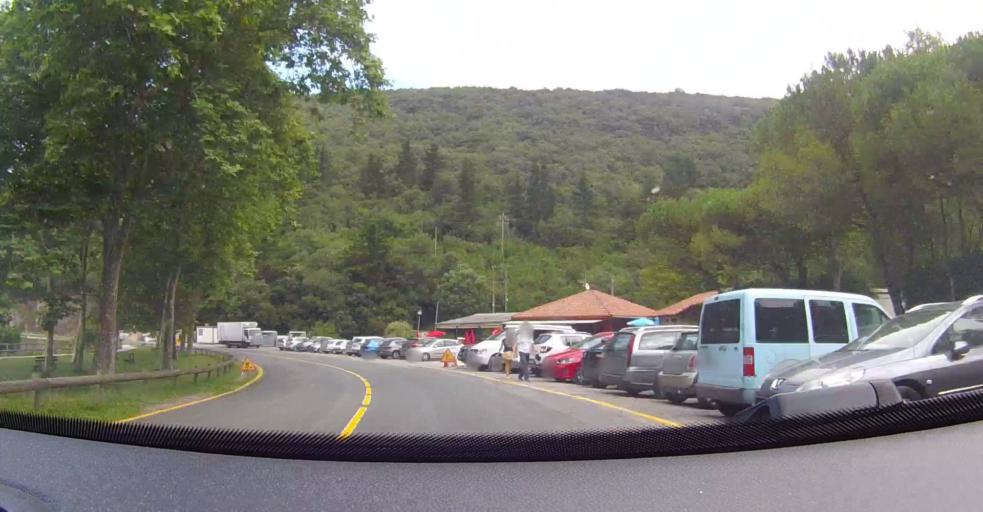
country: ES
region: Basque Country
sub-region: Bizkaia
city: Mundaka
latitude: 43.3950
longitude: -2.6806
